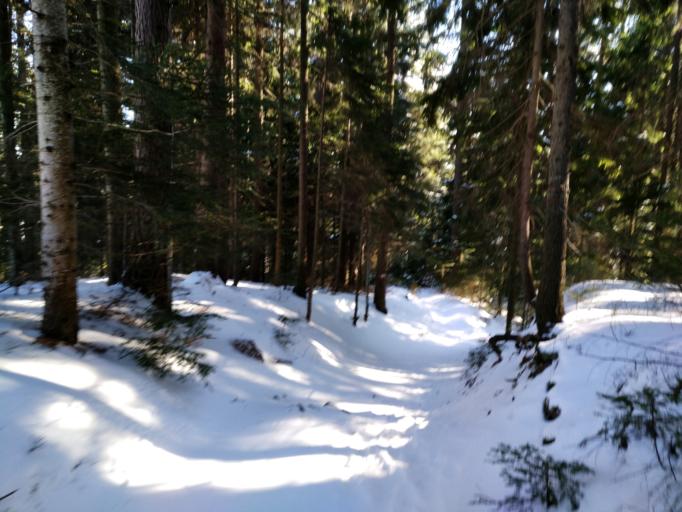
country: AT
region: Styria
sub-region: Politischer Bezirk Hartberg-Fuerstenfeld
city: Sankt Jakob im Walde
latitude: 47.4745
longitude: 15.7878
